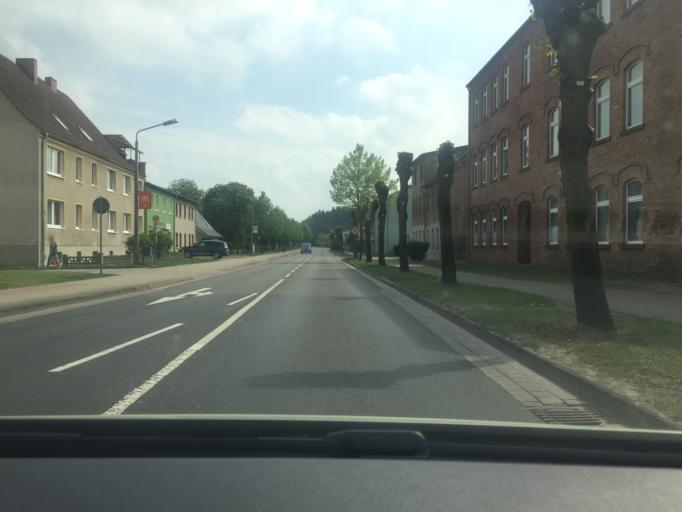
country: DE
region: Mecklenburg-Vorpommern
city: Torgelow
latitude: 53.6282
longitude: 14.0160
